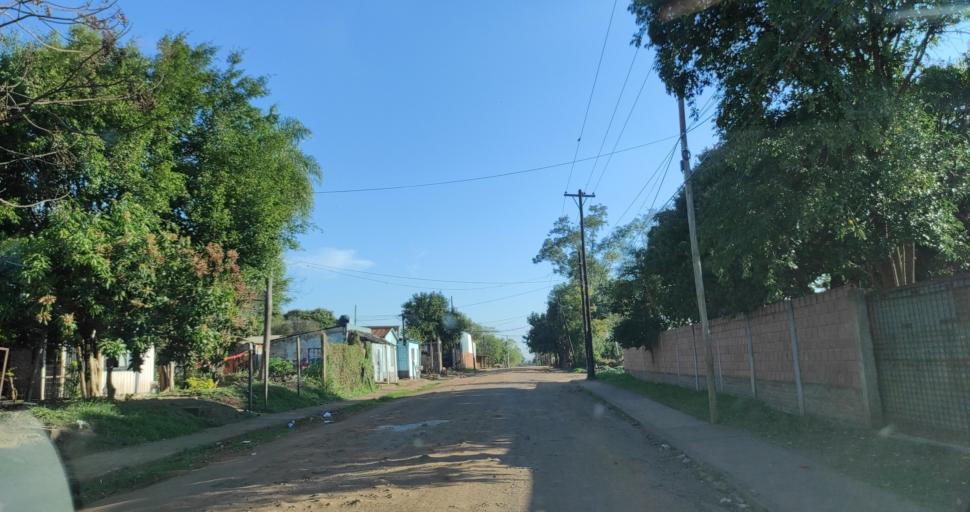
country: AR
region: Misiones
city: Garupa
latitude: -27.4499
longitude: -55.8627
